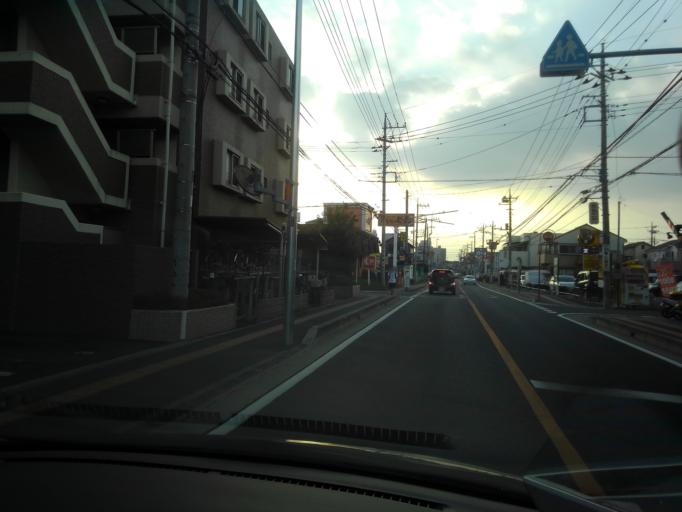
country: JP
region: Saitama
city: Tokorozawa
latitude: 35.7903
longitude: 139.4838
